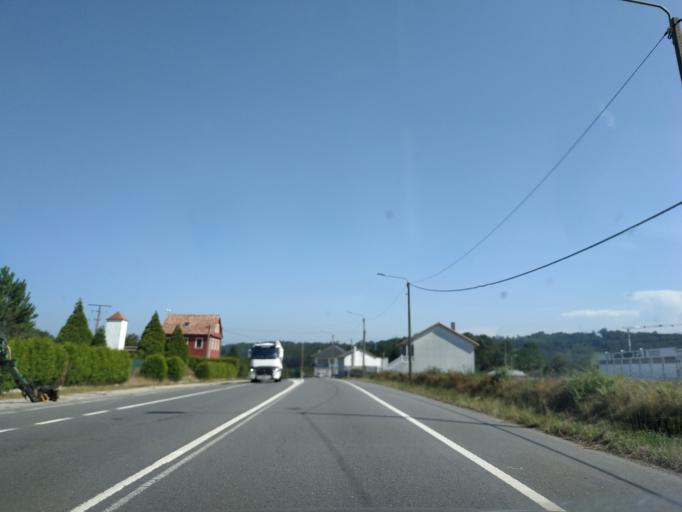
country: ES
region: Galicia
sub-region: Provincia da Coruna
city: Carballo
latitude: 43.2304
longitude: -8.6588
